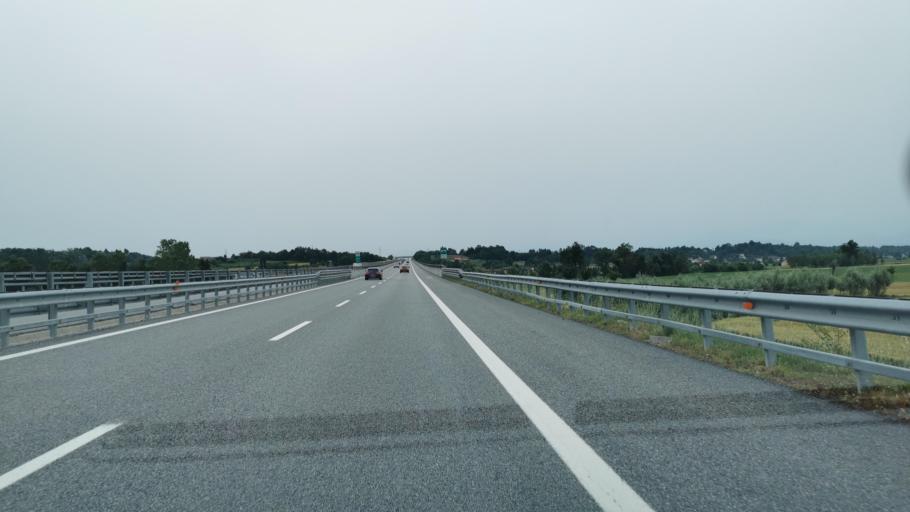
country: IT
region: Piedmont
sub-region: Provincia di Cuneo
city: Bene Vagienna
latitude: 44.5148
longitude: 7.8013
